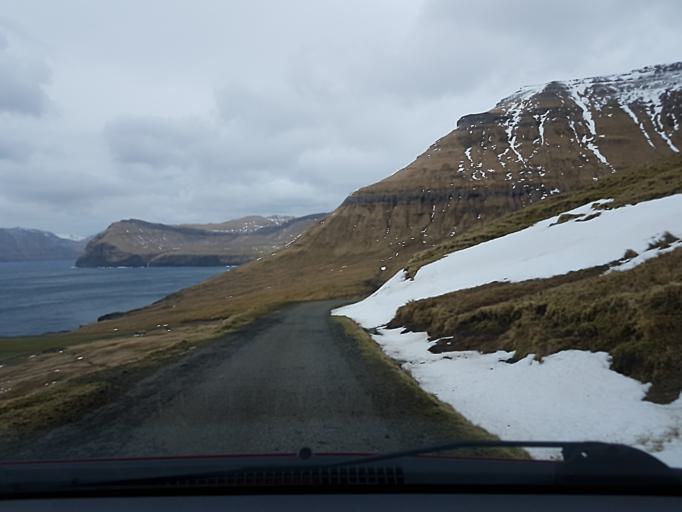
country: FO
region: Streymoy
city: Kollafjordhur
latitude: 62.0203
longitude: -6.9092
